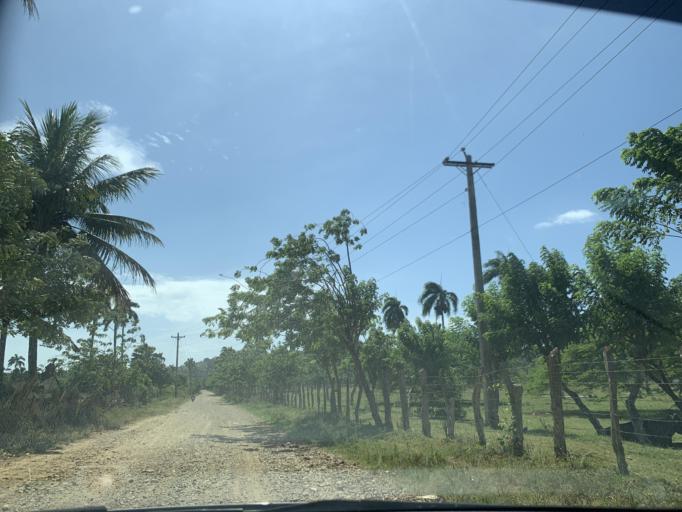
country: DO
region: Puerto Plata
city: Luperon
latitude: 19.8900
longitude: -70.8797
